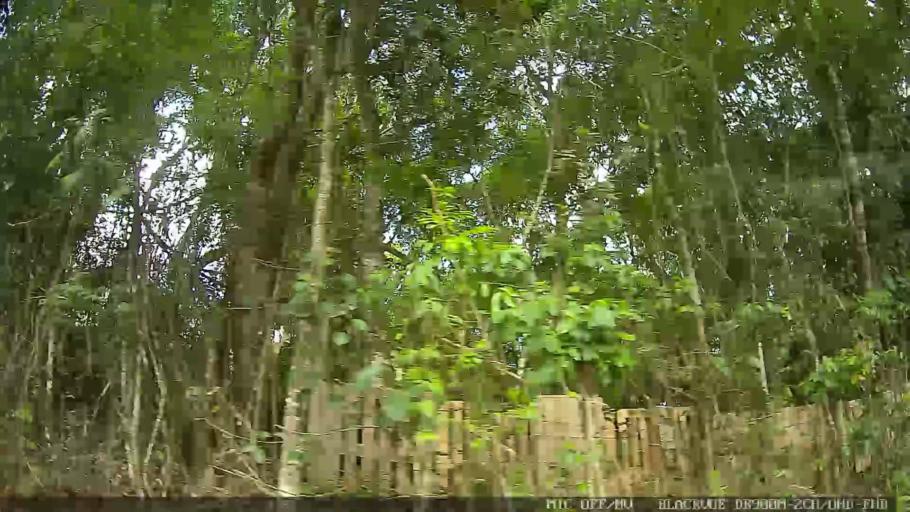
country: BR
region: Sao Paulo
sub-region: Braganca Paulista
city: Braganca Paulista
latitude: -22.9834
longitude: -46.5551
